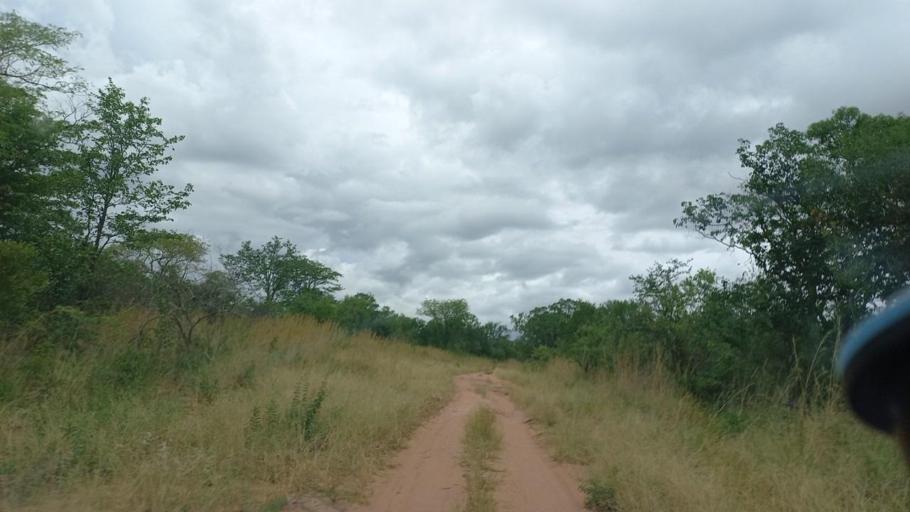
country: ZM
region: Lusaka
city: Luangwa
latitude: -15.5681
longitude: 30.3216
